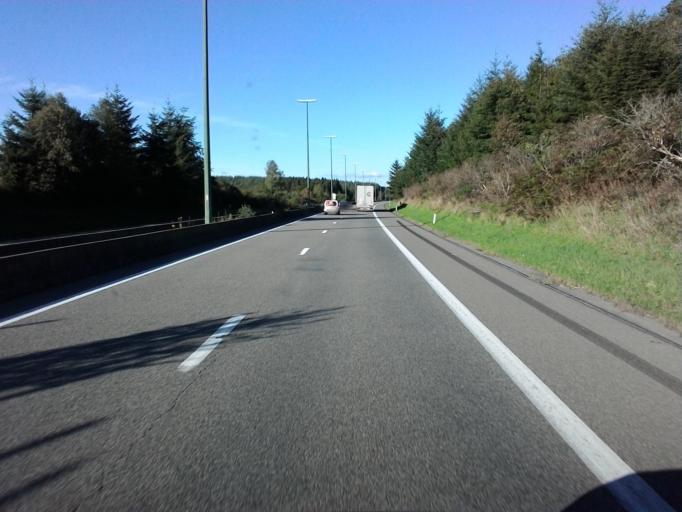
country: BE
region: Wallonia
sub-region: Province du Luxembourg
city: Bastogne
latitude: 50.0348
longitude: 5.7028
